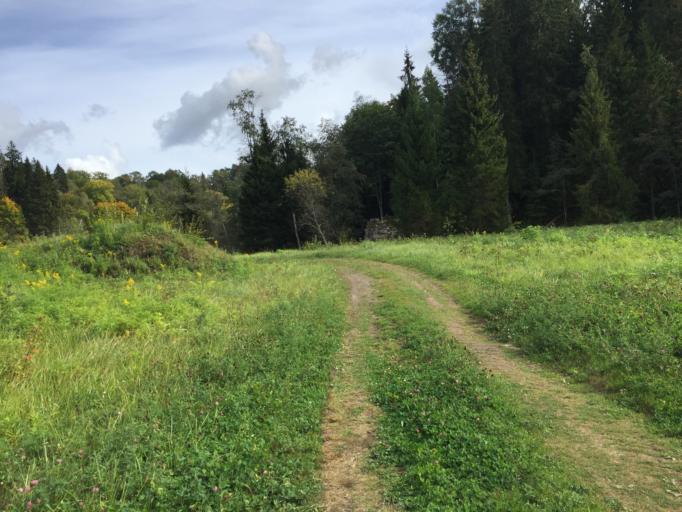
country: LV
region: Ligatne
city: Ligatne
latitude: 57.2315
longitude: 25.0468
